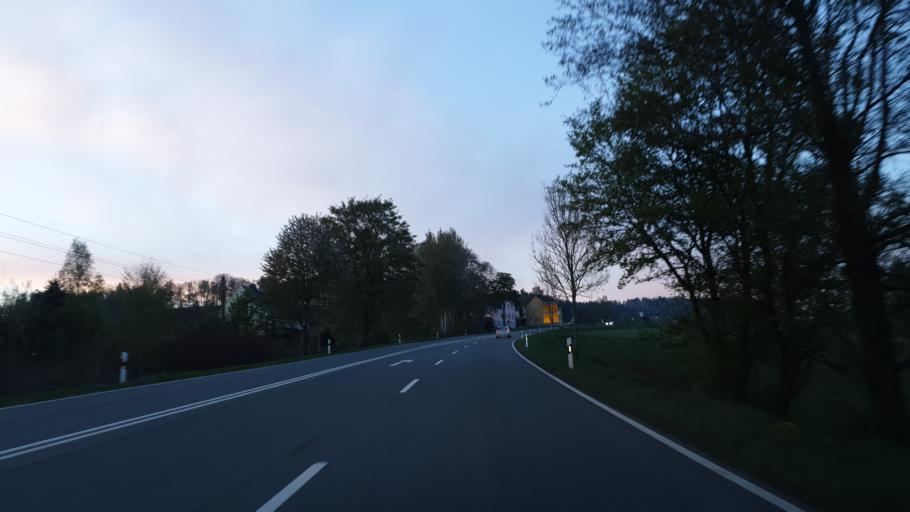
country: DE
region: Saxony
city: Lossnitz
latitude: 50.6384
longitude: 12.7343
